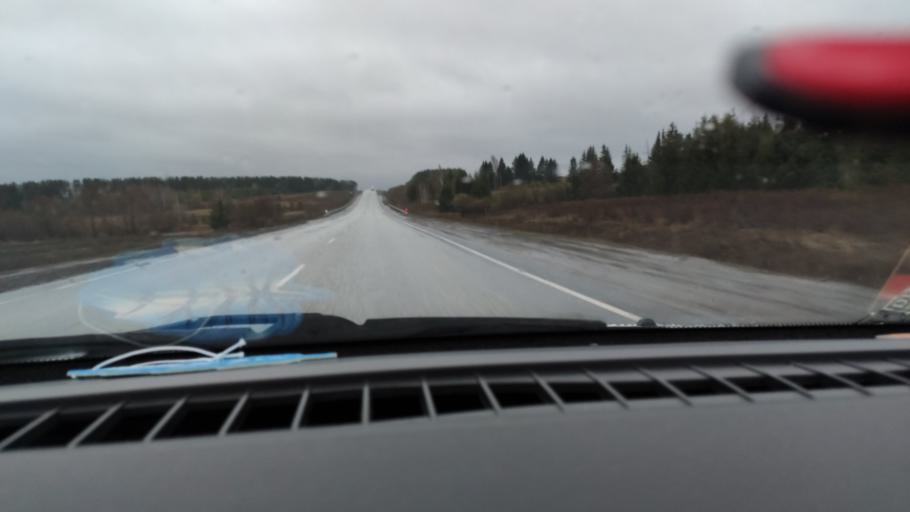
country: RU
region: Udmurtiya
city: Alnashi
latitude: 56.0573
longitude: 52.3933
